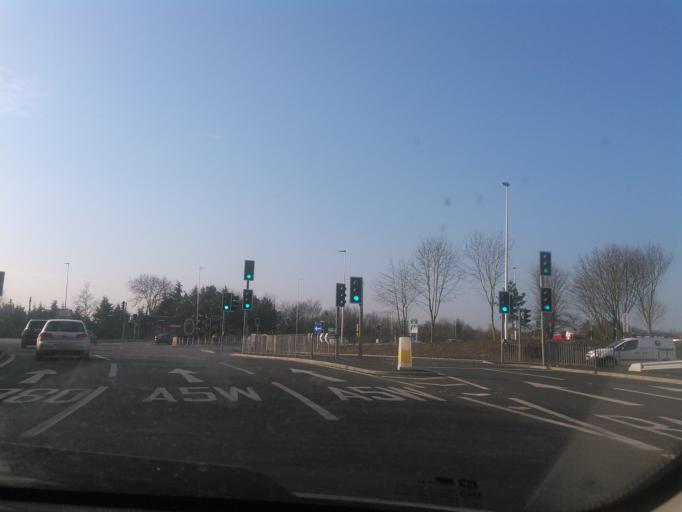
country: GB
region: England
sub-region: Shropshire
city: Berrington
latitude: 52.6928
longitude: -2.7097
